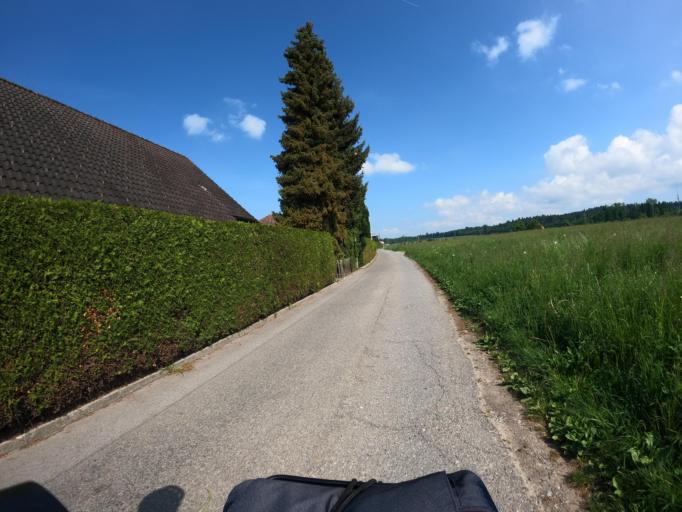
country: CH
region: Zug
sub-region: Zug
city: Steinhausen
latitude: 47.1961
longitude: 8.4947
